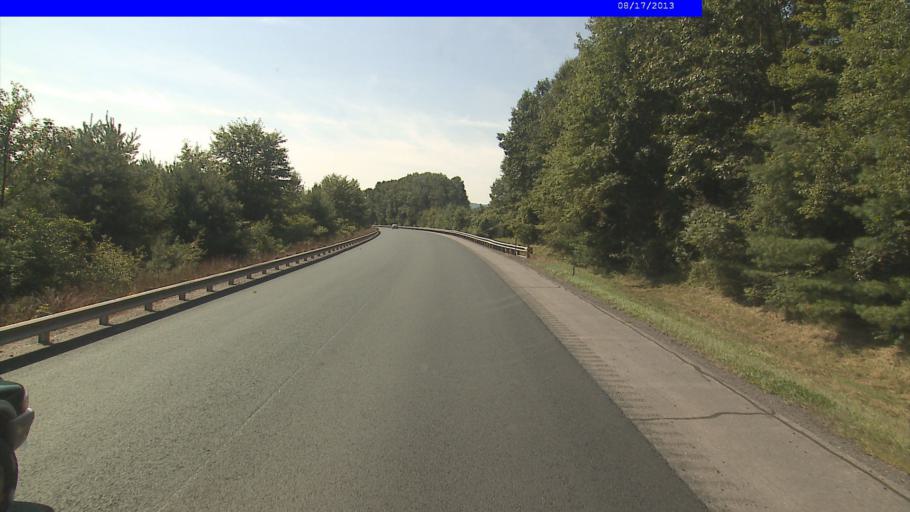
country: US
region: New Hampshire
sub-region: Cheshire County
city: Chesterfield
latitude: 42.9300
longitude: -72.5288
